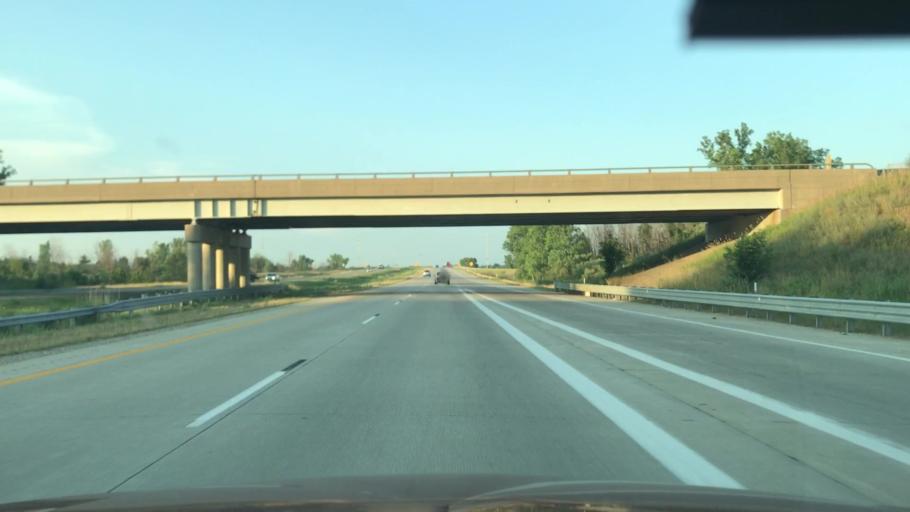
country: US
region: Michigan
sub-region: Ottawa County
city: Holland
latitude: 42.7435
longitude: -86.0722
